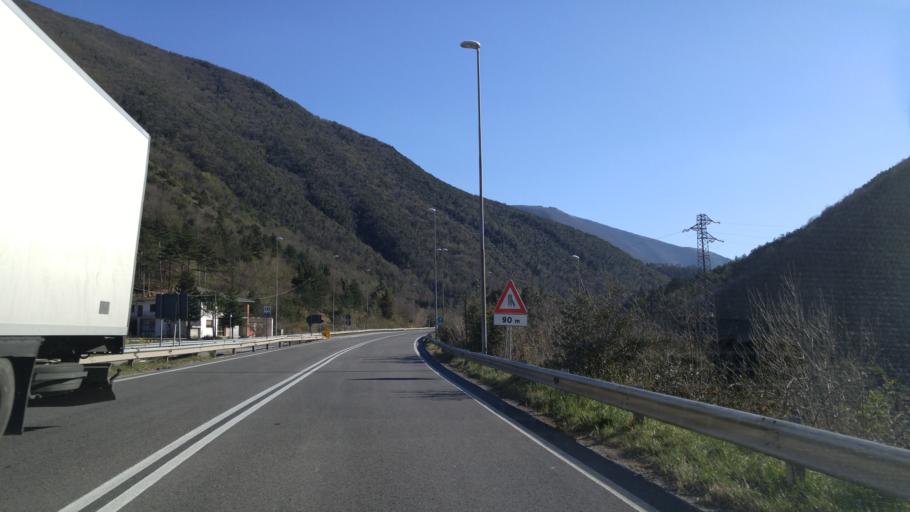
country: IT
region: The Marches
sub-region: Provincia di Pesaro e Urbino
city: Cagli
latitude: 43.5369
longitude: 12.6462
